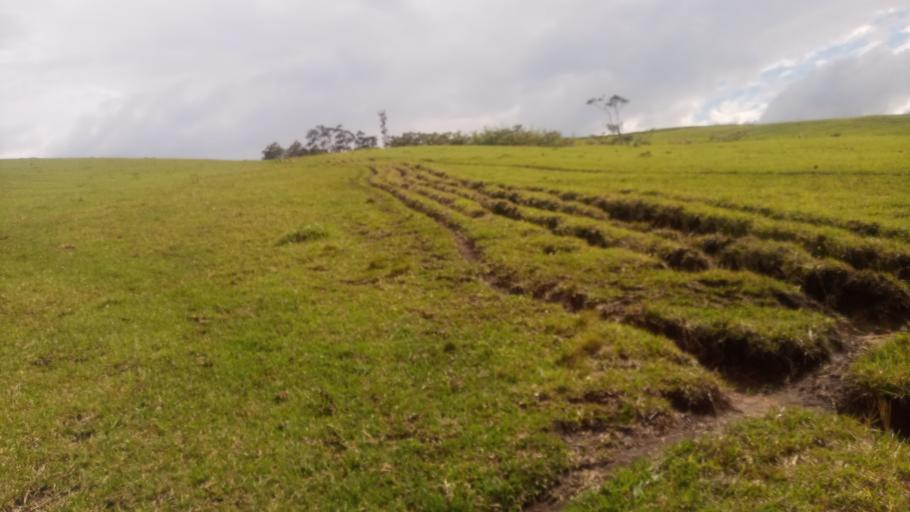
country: CO
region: Valle del Cauca
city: Yotoco
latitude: 3.8843
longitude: -76.4423
